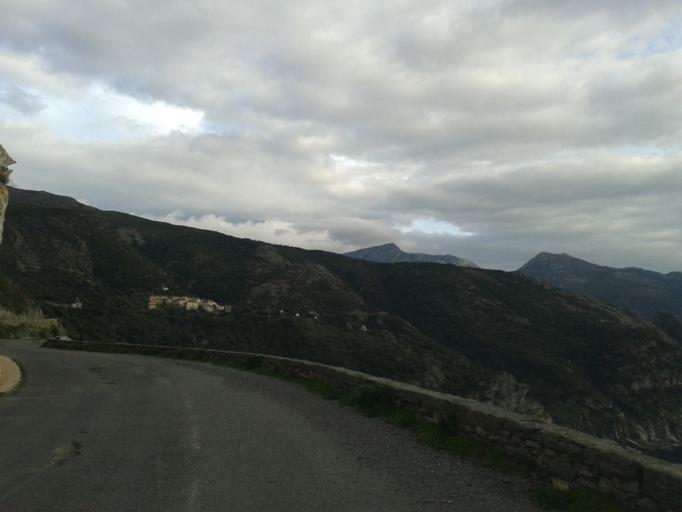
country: FR
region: Corsica
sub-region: Departement de la Haute-Corse
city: Brando
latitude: 42.8935
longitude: 9.3248
